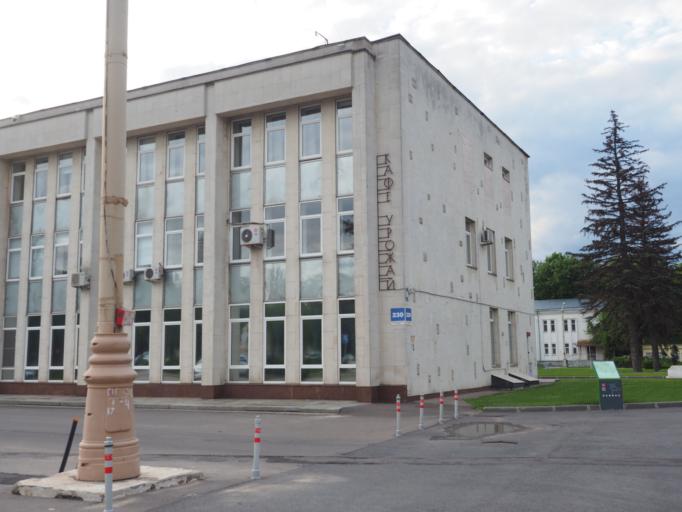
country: RU
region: Moscow
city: Sviblovo
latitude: 55.8313
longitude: 37.6371
